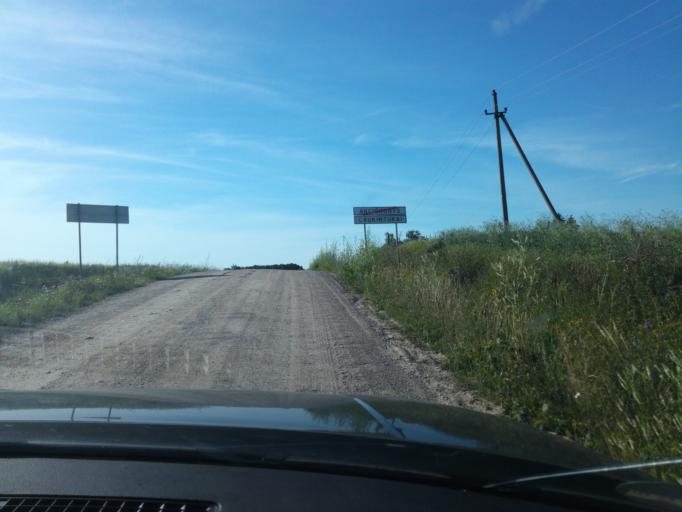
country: LT
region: Alytaus apskritis
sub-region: Alytus
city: Alytus
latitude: 54.3353
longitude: 23.8783
